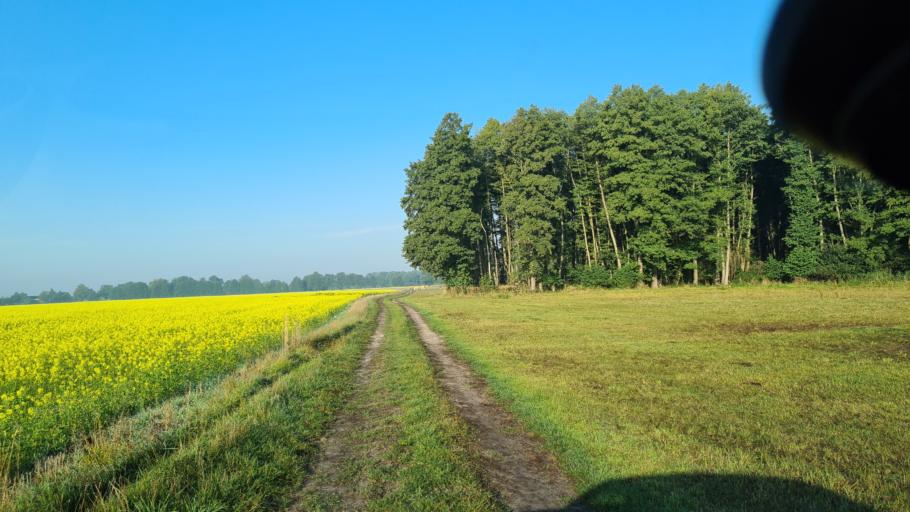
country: DE
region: Brandenburg
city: Schonewalde
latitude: 51.6577
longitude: 13.6139
